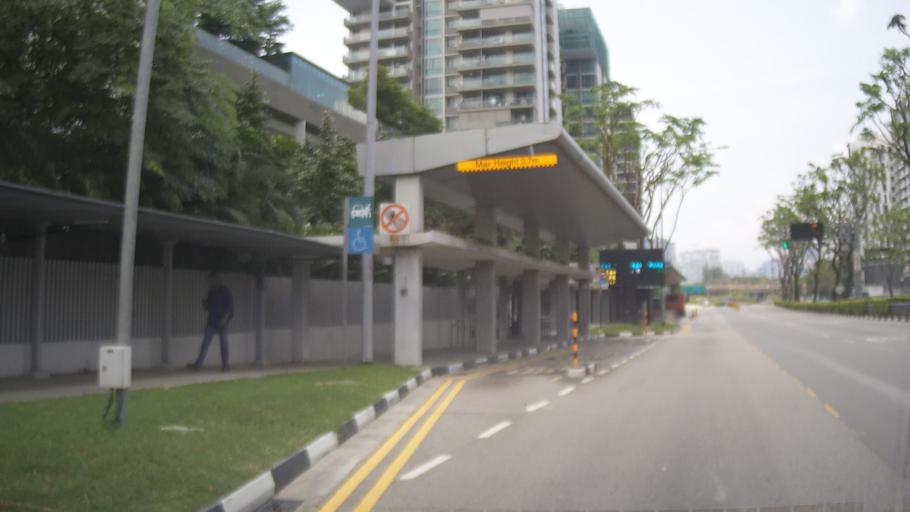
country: SG
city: Singapore
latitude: 1.3320
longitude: 103.8694
